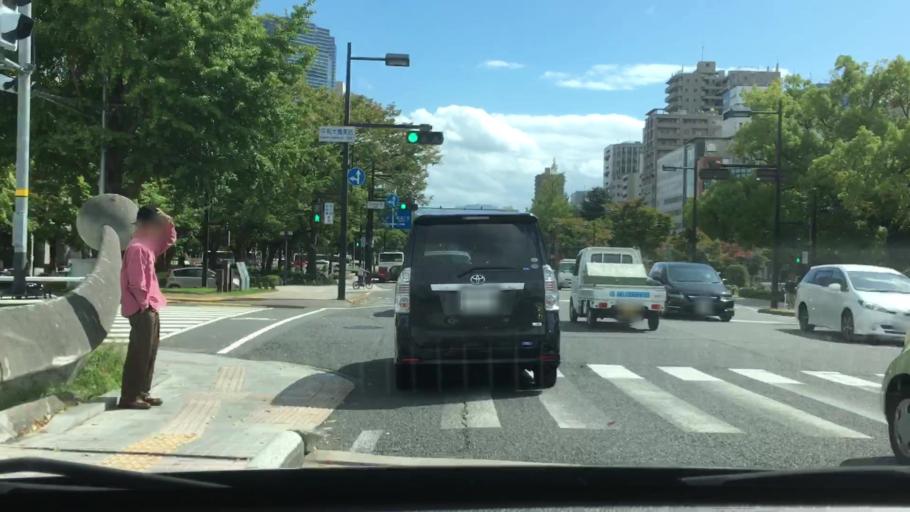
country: JP
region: Hiroshima
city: Hiroshima-shi
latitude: 34.3903
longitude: 132.4541
